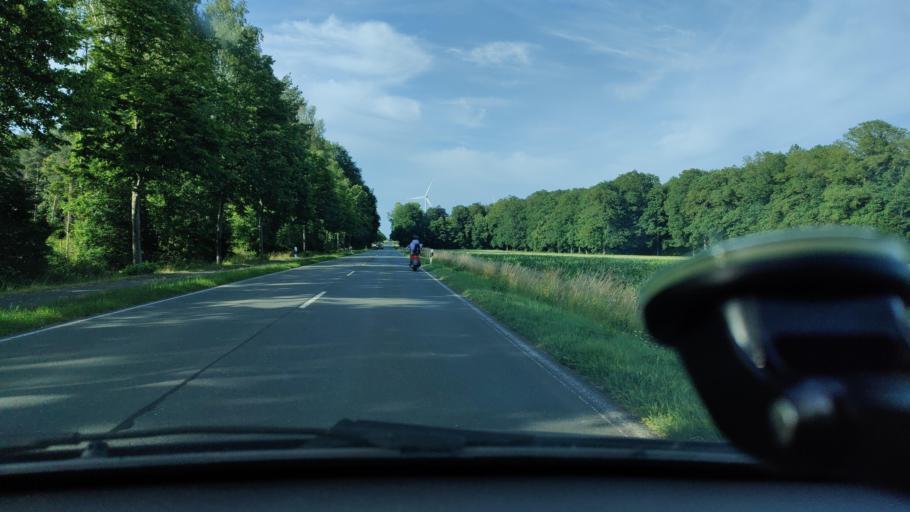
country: DE
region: North Rhine-Westphalia
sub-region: Regierungsbezirk Munster
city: Coesfeld
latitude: 51.9847
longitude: 7.1944
